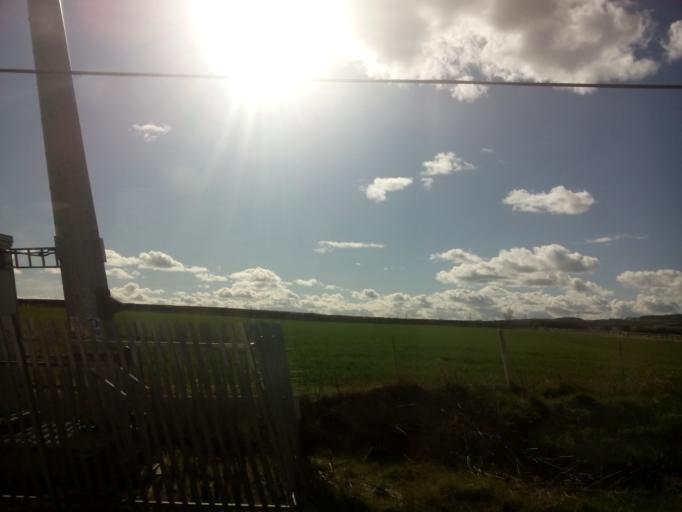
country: GB
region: England
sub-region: County Durham
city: Spennymoor
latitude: 54.7406
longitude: -1.6045
